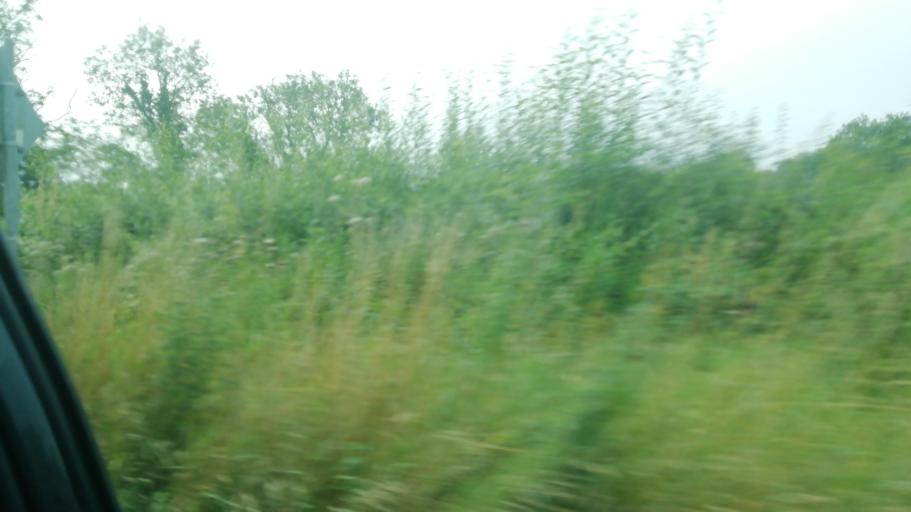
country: IE
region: Leinster
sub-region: Kilkenny
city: Callan
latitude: 52.5512
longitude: -7.5407
